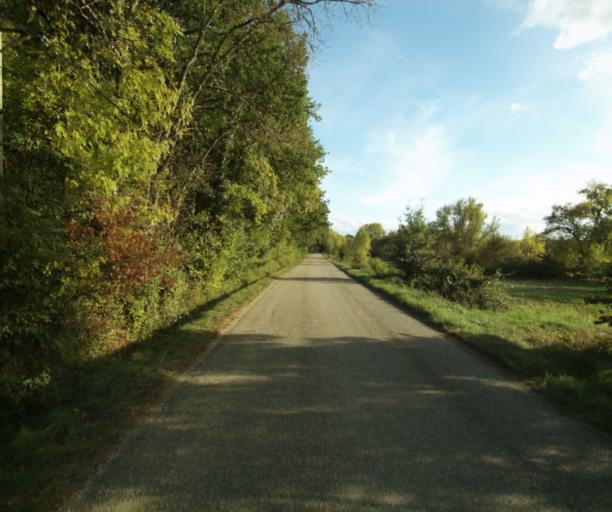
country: FR
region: Midi-Pyrenees
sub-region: Departement du Gers
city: Gondrin
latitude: 43.8946
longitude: 0.2966
